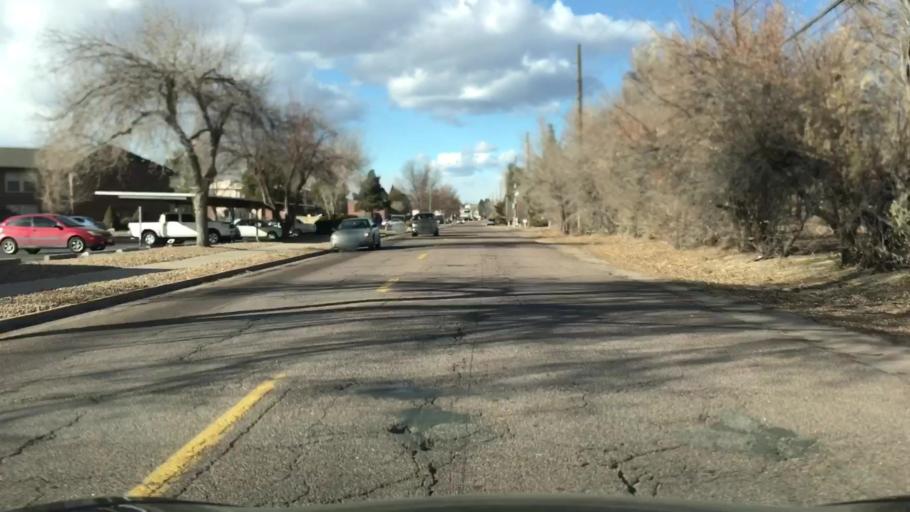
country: US
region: Colorado
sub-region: Arapahoe County
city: Glendale
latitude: 39.6924
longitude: -104.8995
